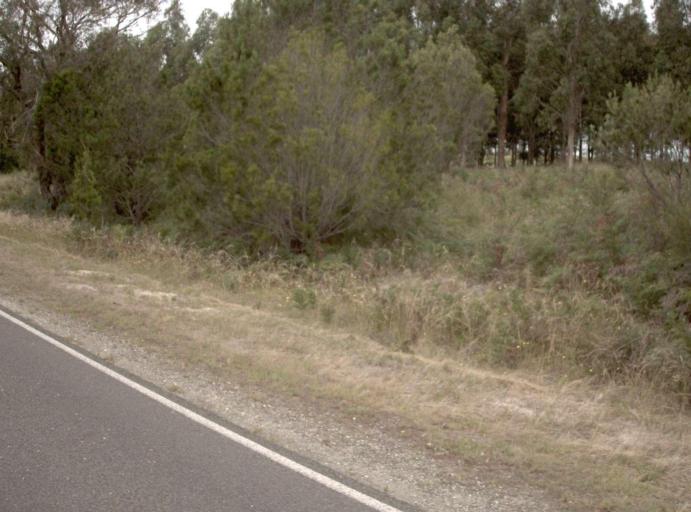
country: AU
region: Victoria
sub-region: Wellington
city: Sale
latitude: -38.1934
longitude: 147.2876
